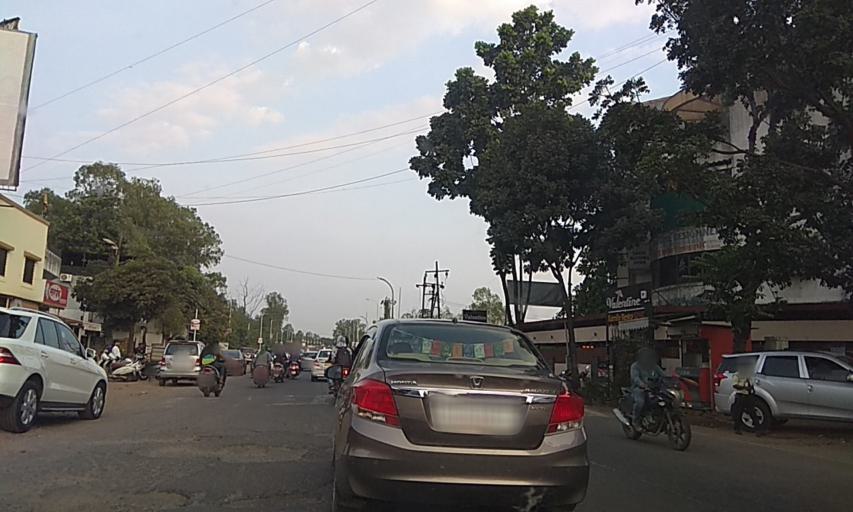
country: IN
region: Maharashtra
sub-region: Pune Division
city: Pimpri
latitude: 18.5882
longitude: 73.7846
